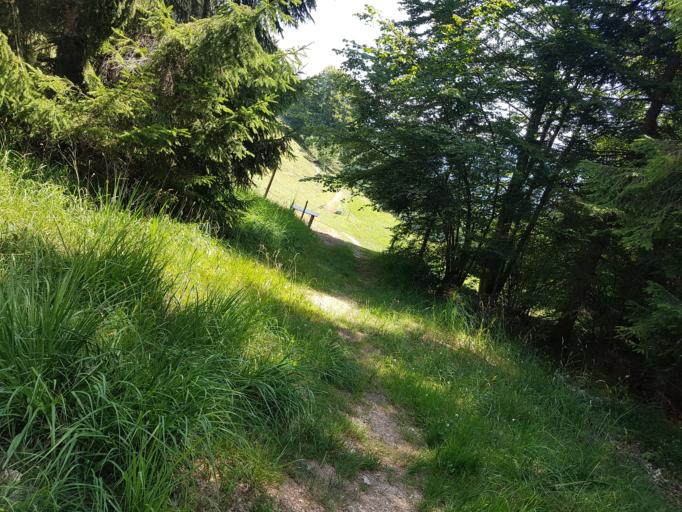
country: DE
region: Bavaria
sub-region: Upper Bavaria
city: Berchtesgaden
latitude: 47.6486
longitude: 13.0096
